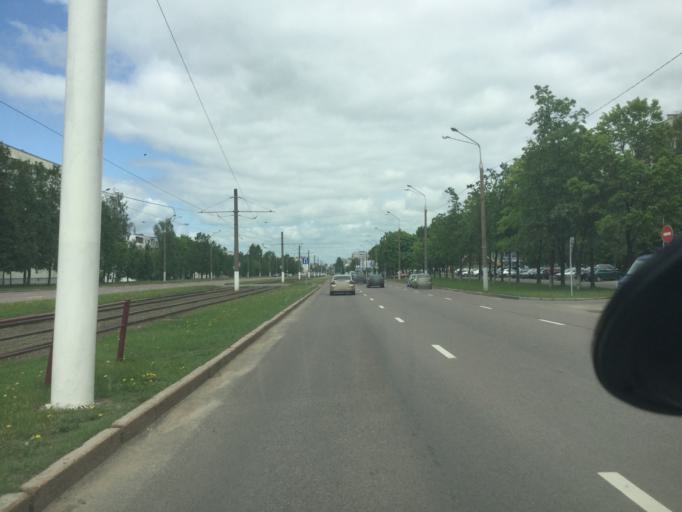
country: BY
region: Vitebsk
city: Vitebsk
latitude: 55.1792
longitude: 30.2290
